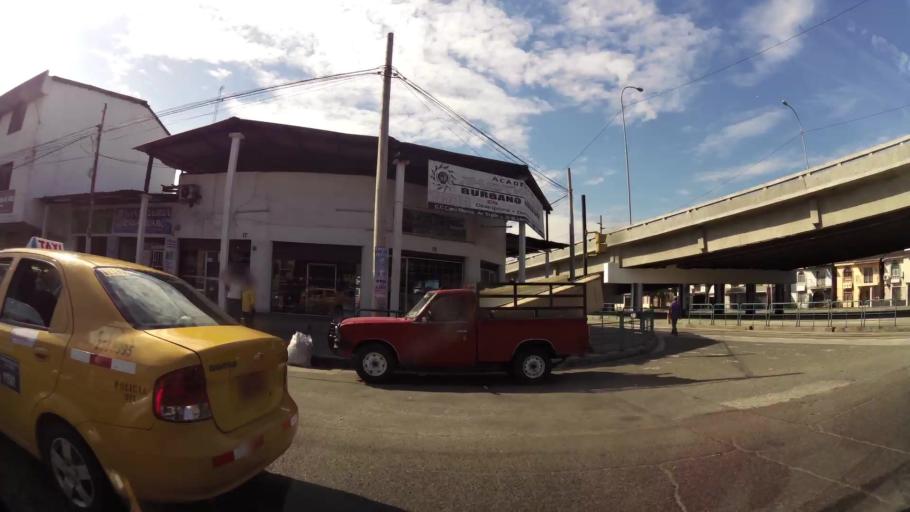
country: EC
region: Guayas
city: Guayaquil
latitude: -2.2225
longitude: -79.8988
